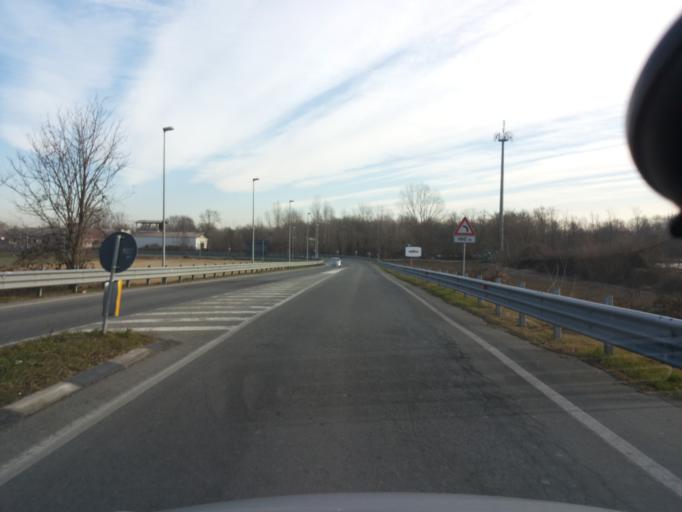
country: IT
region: Piedmont
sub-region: Provincia di Vercelli
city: Arborio
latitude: 45.4913
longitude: 8.3905
